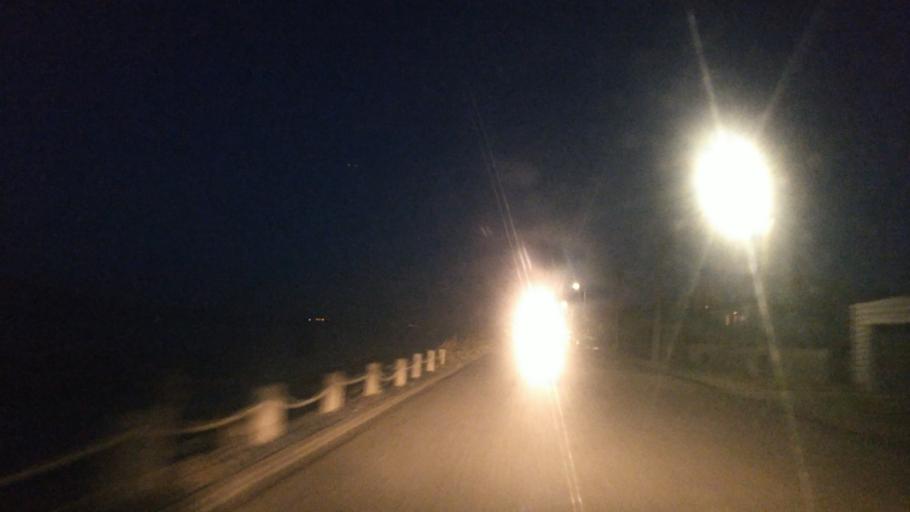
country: NZ
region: Wellington
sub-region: Kapiti Coast District
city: Paraparaumu
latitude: -40.9838
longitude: 174.9524
